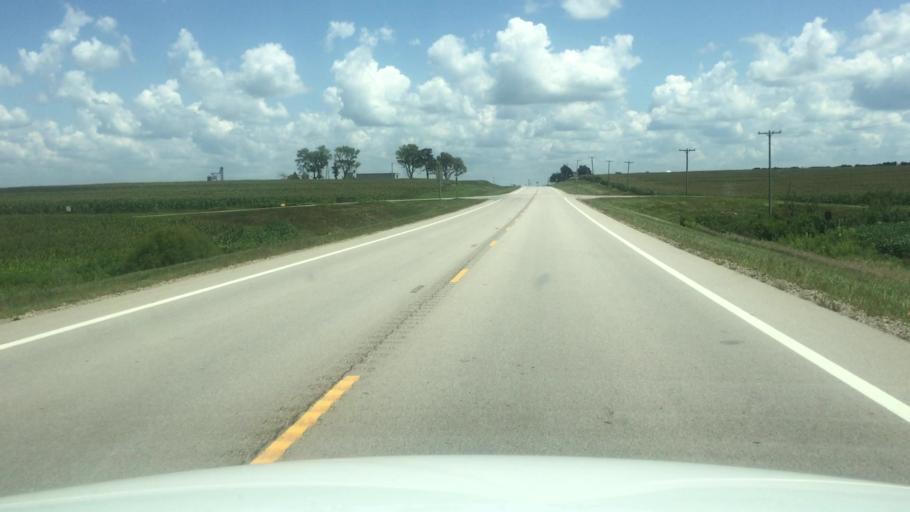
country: US
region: Kansas
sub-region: Brown County
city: Horton
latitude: 39.6673
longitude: -95.4354
